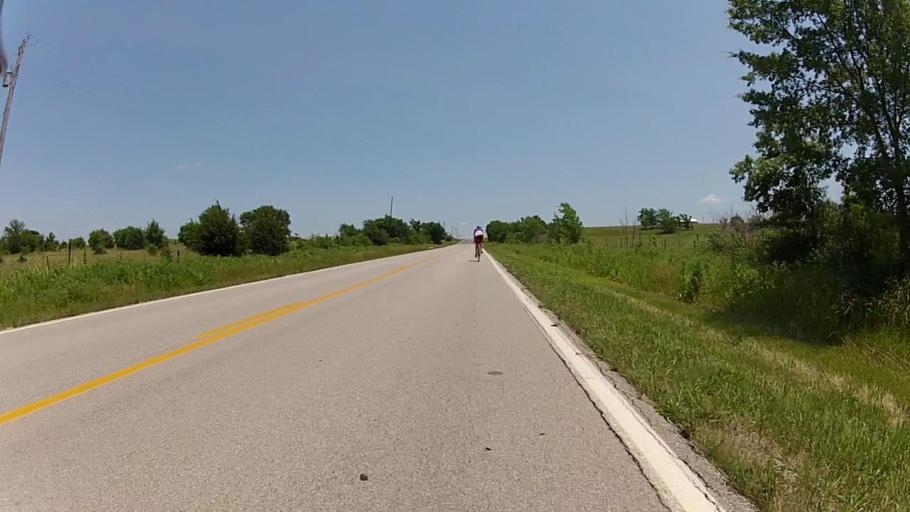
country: US
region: Kansas
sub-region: Montgomery County
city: Cherryvale
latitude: 37.1938
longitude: -95.5346
